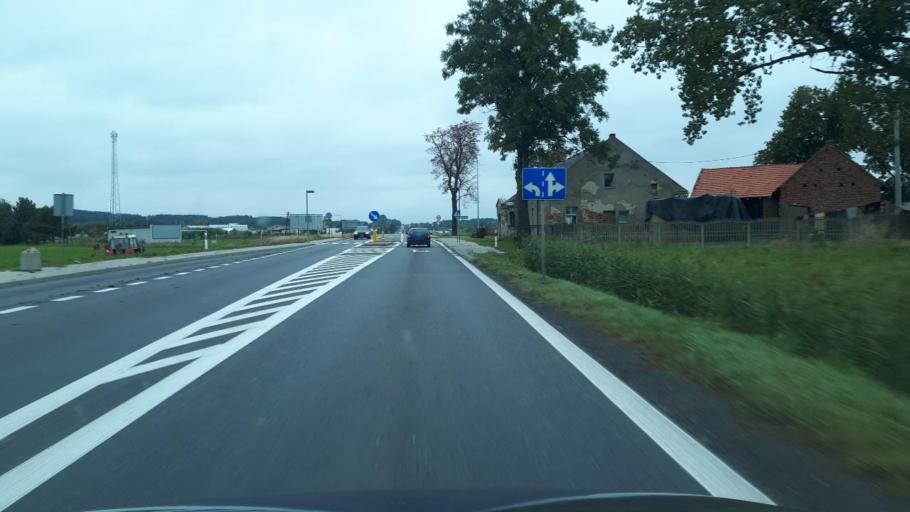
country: PL
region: Greater Poland Voivodeship
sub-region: Powiat ostrzeszowski
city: Ostrzeszow
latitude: 51.3863
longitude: 17.9486
